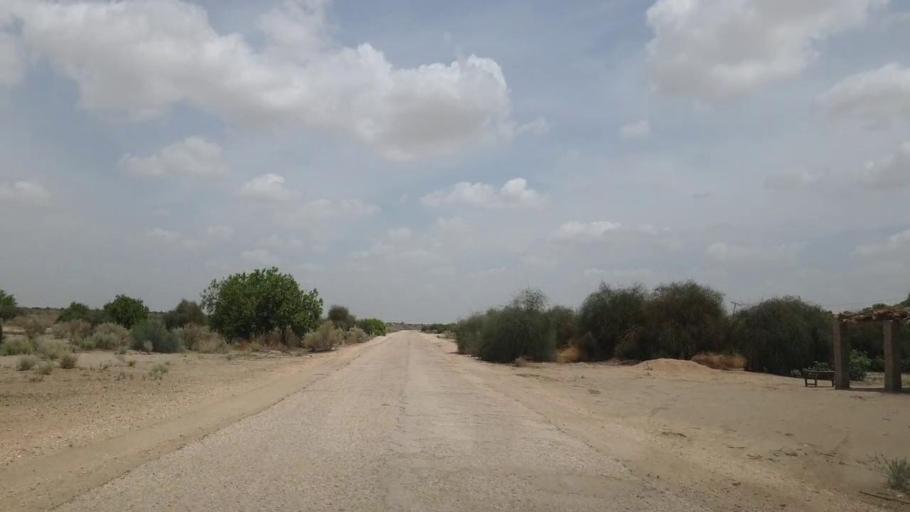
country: PK
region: Sindh
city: Kot Diji
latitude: 27.2030
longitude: 69.1454
